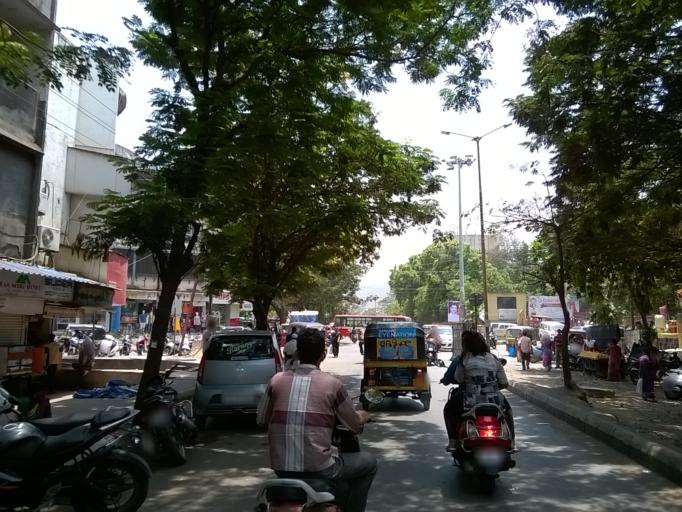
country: IN
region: Maharashtra
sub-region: Raigarh
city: Panvel
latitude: 18.9880
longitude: 73.1126
